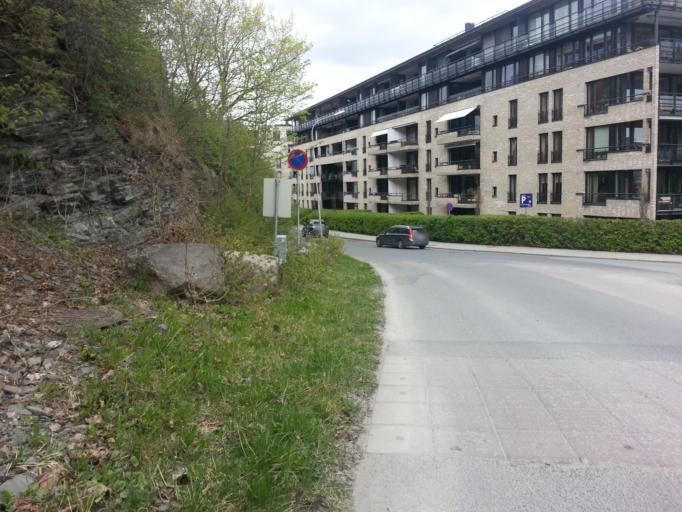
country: NO
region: Akershus
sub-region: Baerum
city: Lysaker
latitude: 59.9091
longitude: 10.6400
